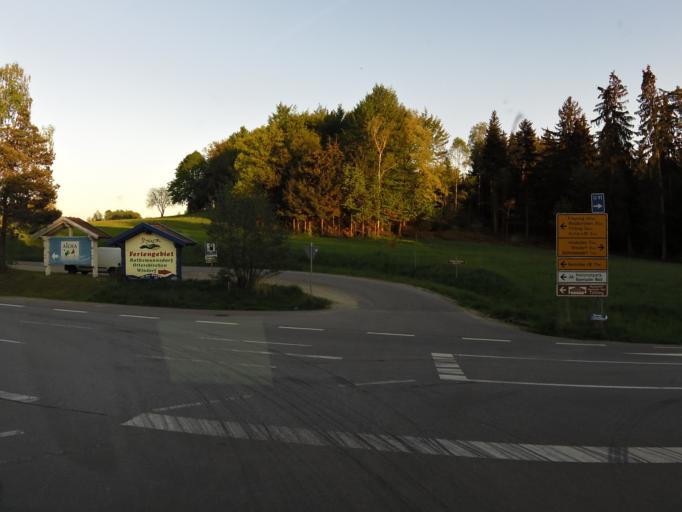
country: DE
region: Bavaria
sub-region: Lower Bavaria
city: Aicha vorm Wald
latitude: 48.6671
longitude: 13.2603
